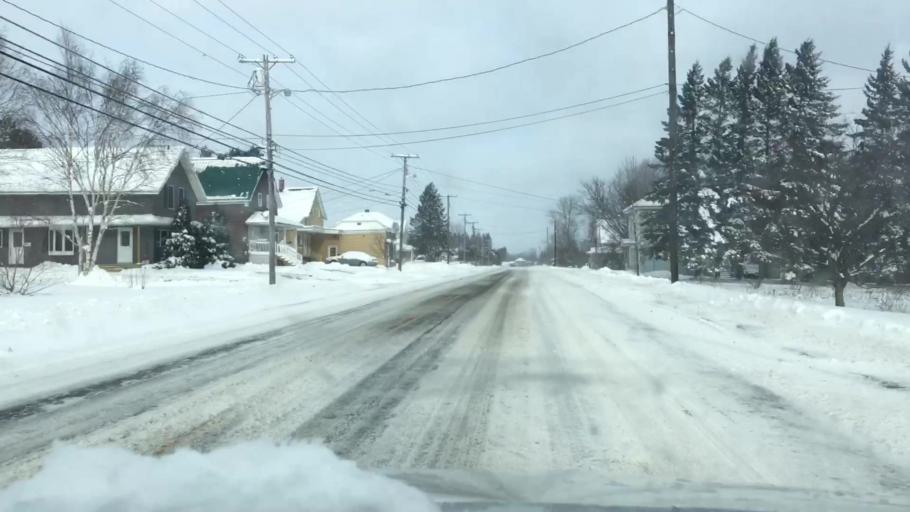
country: US
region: Maine
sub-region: Aroostook County
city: Van Buren
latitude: 47.1719
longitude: -67.9455
